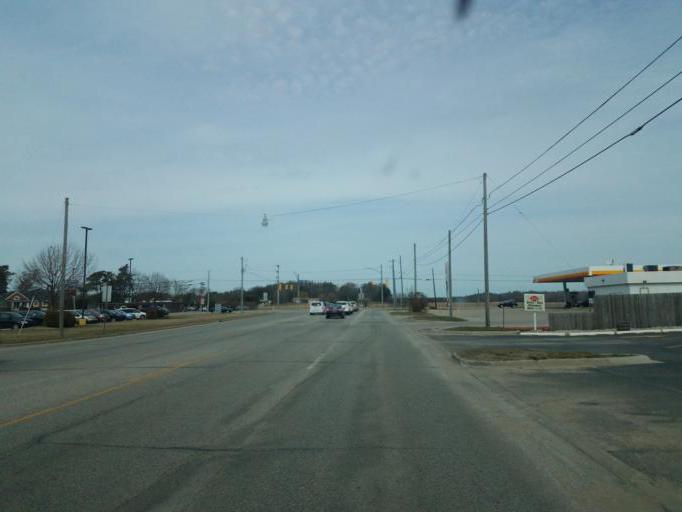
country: US
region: Michigan
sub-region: Mason County
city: Ludington
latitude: 43.9549
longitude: -86.4152
